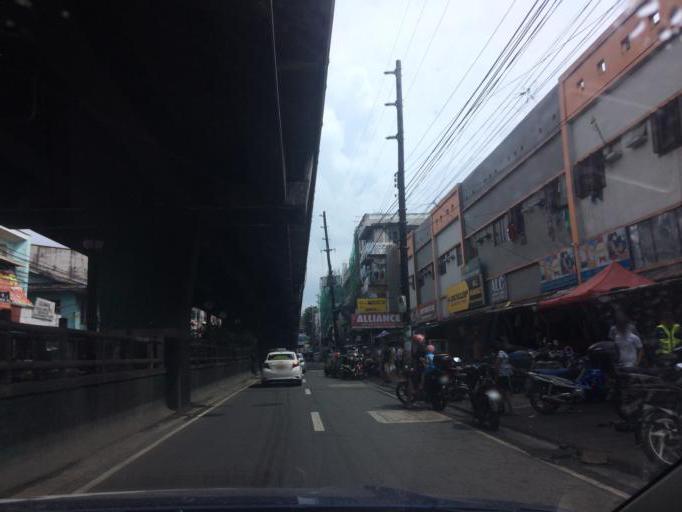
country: PH
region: Metro Manila
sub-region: Makati City
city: Makati City
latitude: 14.5501
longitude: 120.9980
